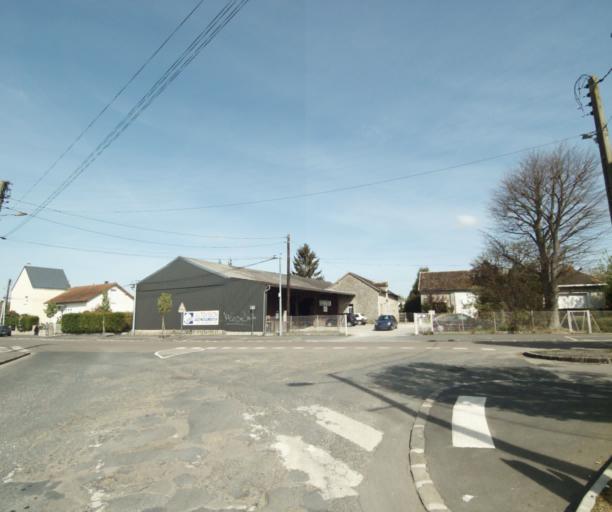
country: FR
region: Ile-de-France
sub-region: Departement de Seine-et-Marne
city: Nangis
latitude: 48.5543
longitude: 3.0243
